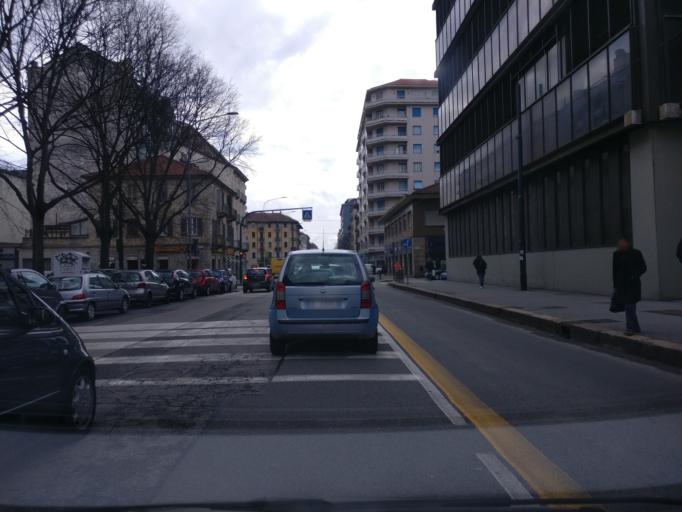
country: IT
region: Piedmont
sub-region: Provincia di Torino
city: Turin
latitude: 45.0397
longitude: 7.6700
